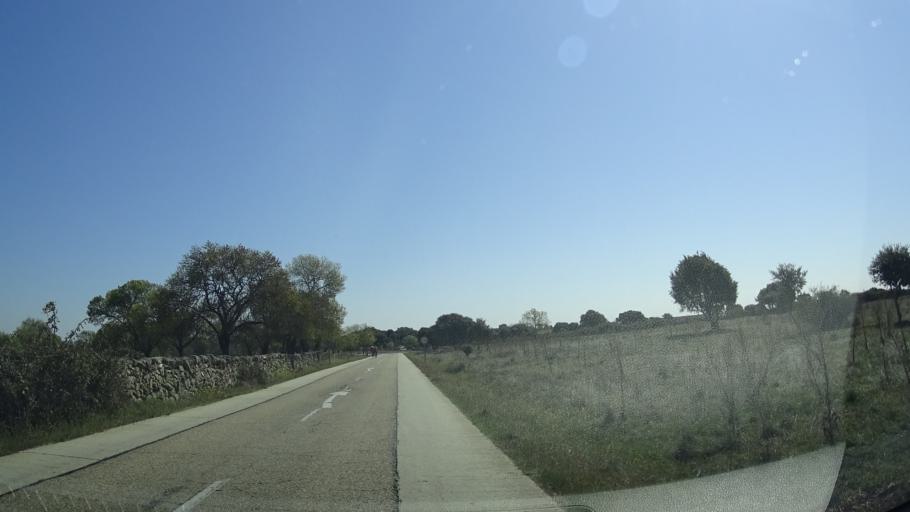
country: ES
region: Madrid
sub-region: Provincia de Madrid
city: Colmenar Viejo
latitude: 40.6443
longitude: -3.8337
